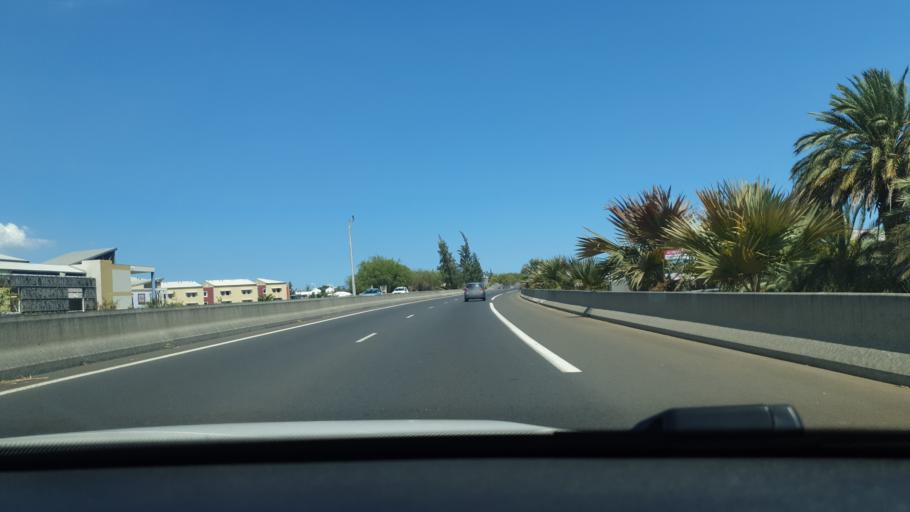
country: RE
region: Reunion
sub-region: Reunion
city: Saint-Louis
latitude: -21.2867
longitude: 55.4005
